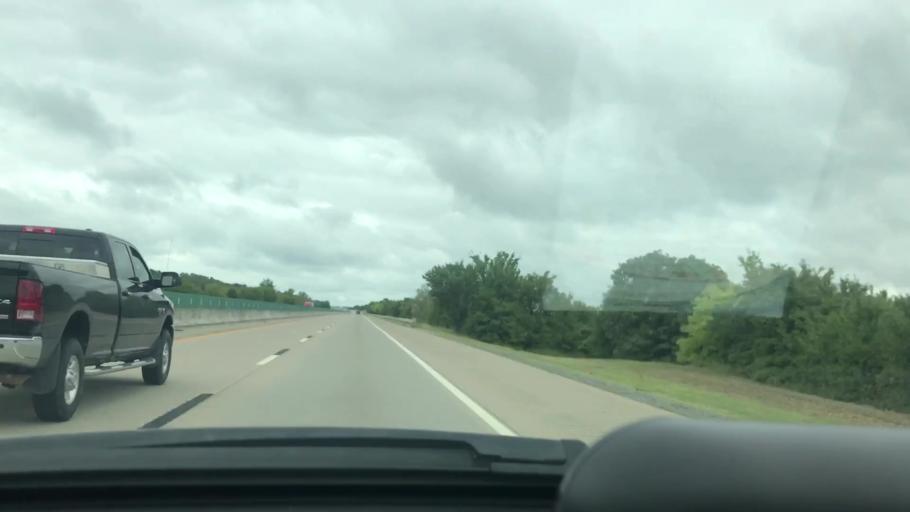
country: US
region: Oklahoma
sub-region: Pittsburg County
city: Krebs
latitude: 35.0243
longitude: -95.7159
